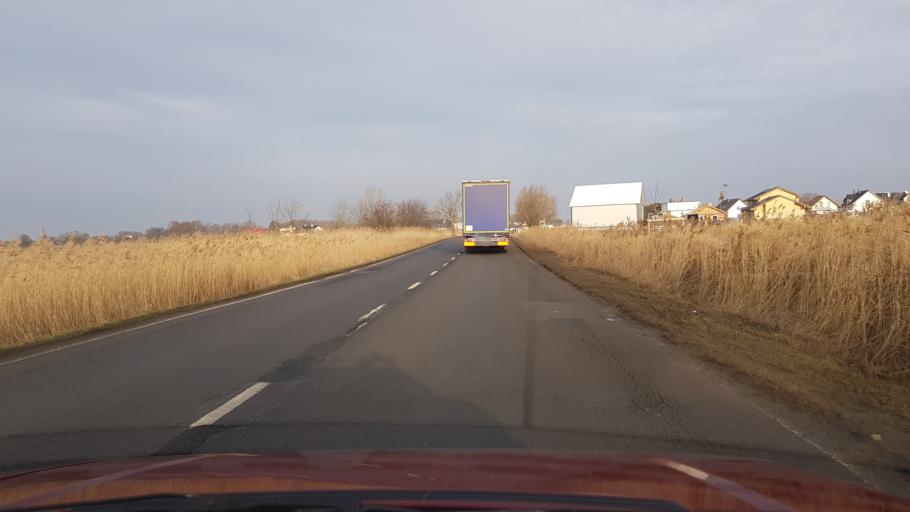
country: PL
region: West Pomeranian Voivodeship
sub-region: Powiat policki
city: Police
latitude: 53.5058
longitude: 14.5734
